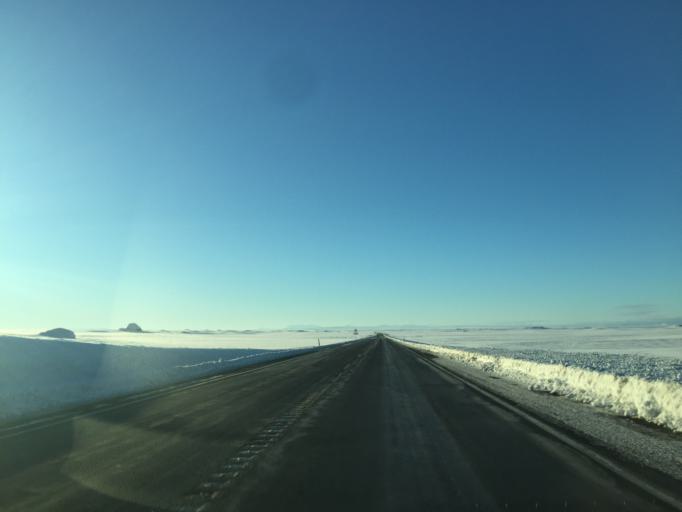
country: US
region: Washington
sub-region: Grant County
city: Soap Lake
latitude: 47.6199
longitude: -119.4274
